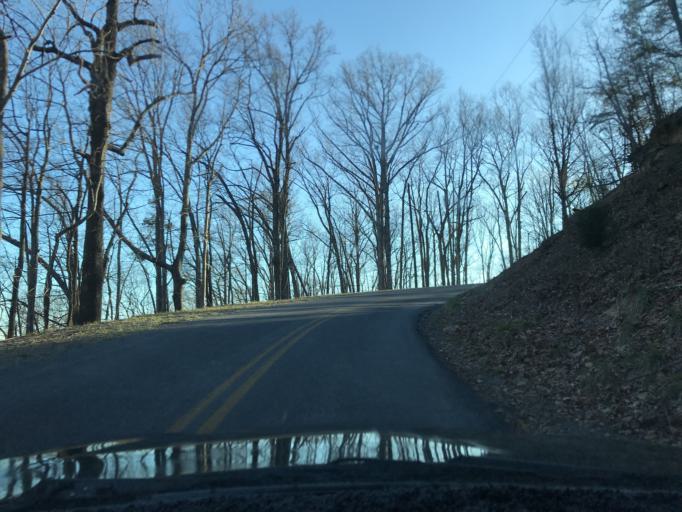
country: US
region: Virginia
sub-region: Botetourt County
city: Buchanan
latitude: 37.4780
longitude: -79.6592
